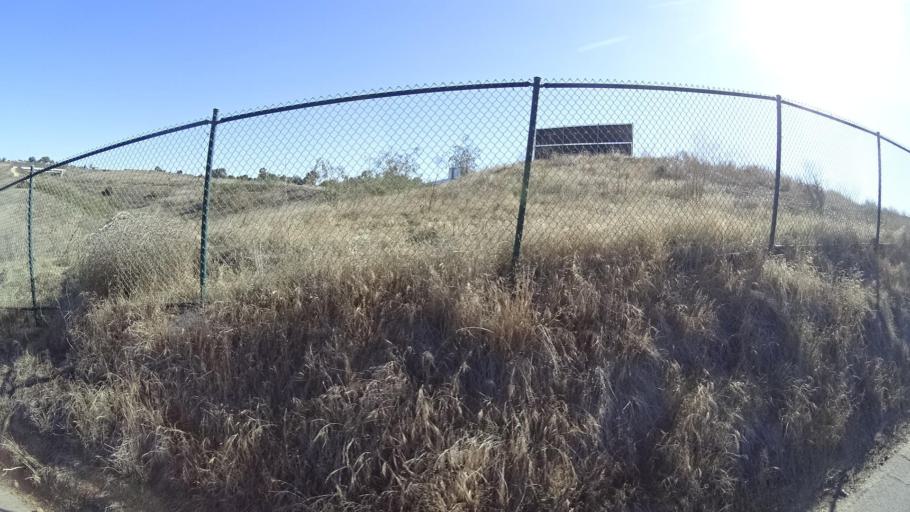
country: US
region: California
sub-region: San Diego County
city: Bonita
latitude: 32.6789
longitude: -117.0085
